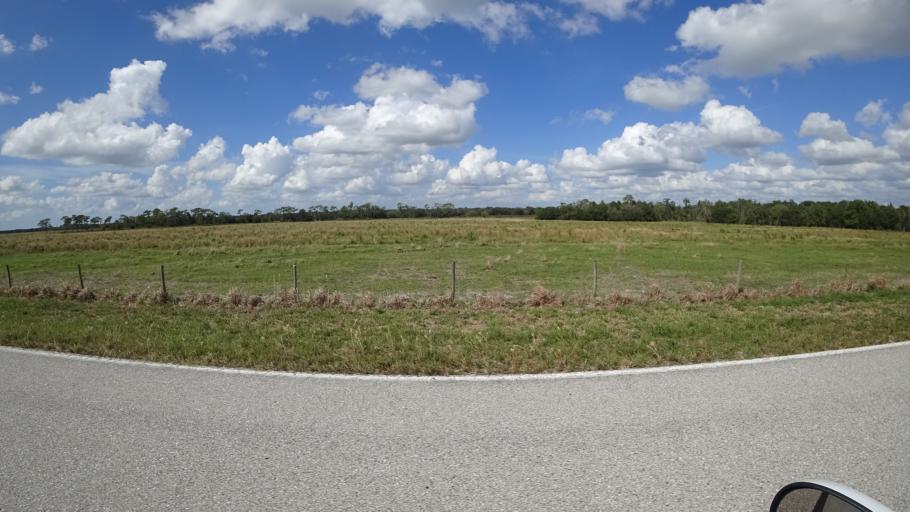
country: US
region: Florida
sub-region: Sarasota County
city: Lake Sarasota
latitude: 27.3202
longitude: -82.1715
